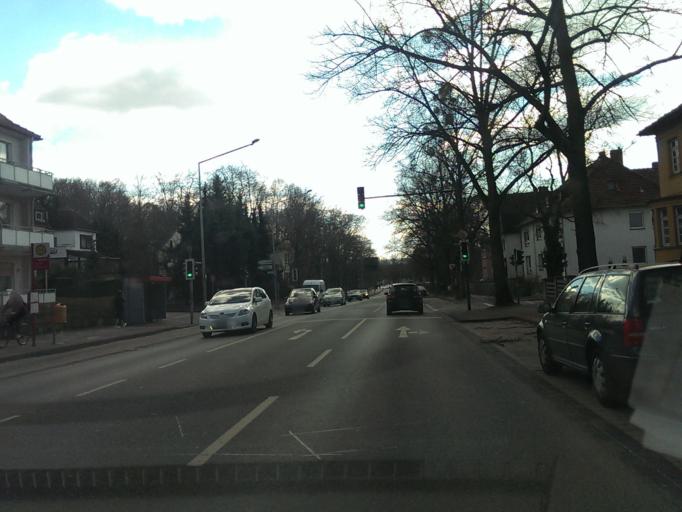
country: DE
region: Lower Saxony
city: Hildesheim
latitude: 52.1405
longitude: 9.9564
